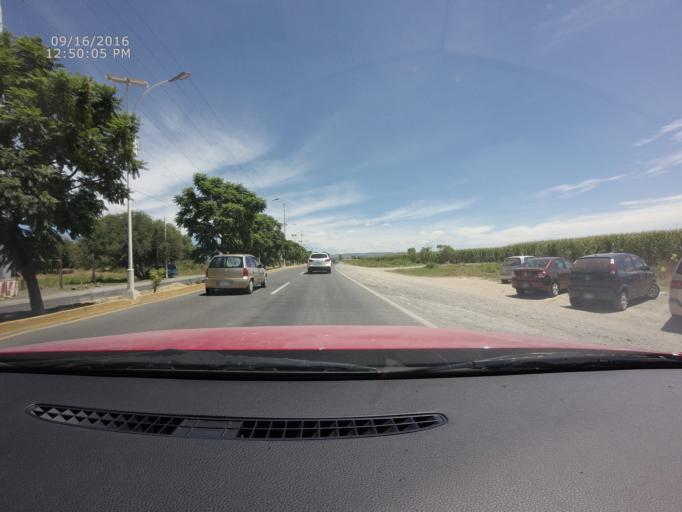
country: MX
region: Queretaro
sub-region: Colon
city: Purisima de Cubos (La Purisima)
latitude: 20.6013
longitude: -100.1719
